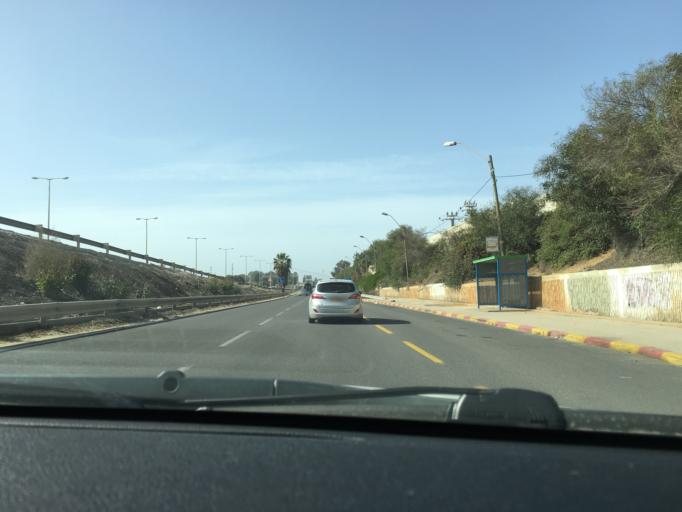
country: IL
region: Tel Aviv
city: Ramat HaSharon
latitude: 32.1256
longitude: 34.8544
